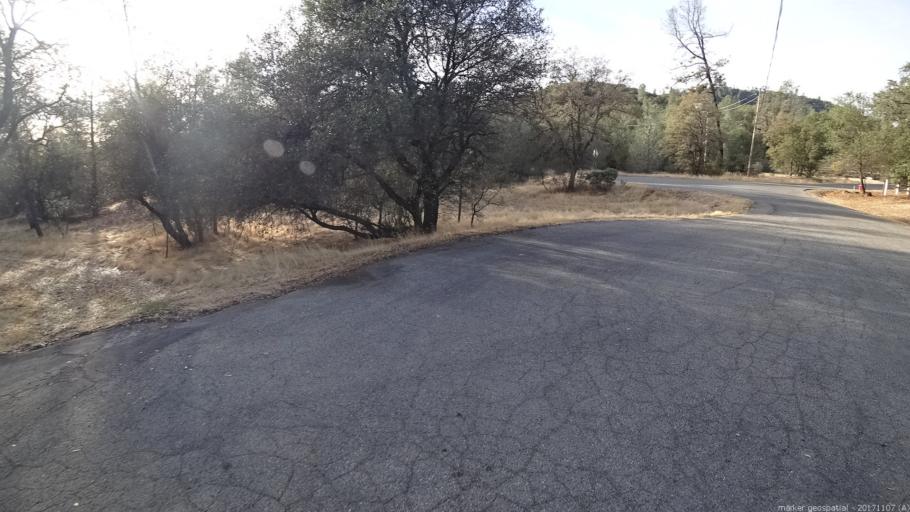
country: US
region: California
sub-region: Shasta County
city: Shasta
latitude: 40.5246
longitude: -122.4855
